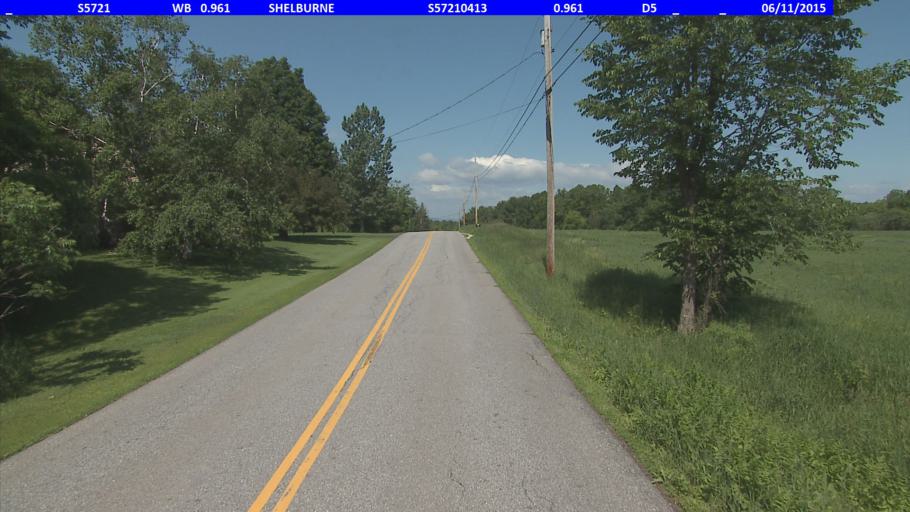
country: US
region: Vermont
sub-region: Chittenden County
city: Hinesburg
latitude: 44.3643
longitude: -73.2019
